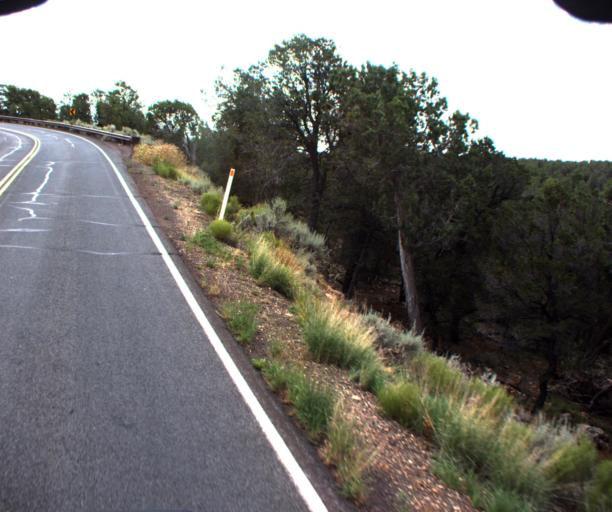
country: US
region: Arizona
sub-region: Coconino County
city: Grand Canyon
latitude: 36.0108
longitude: -111.8758
